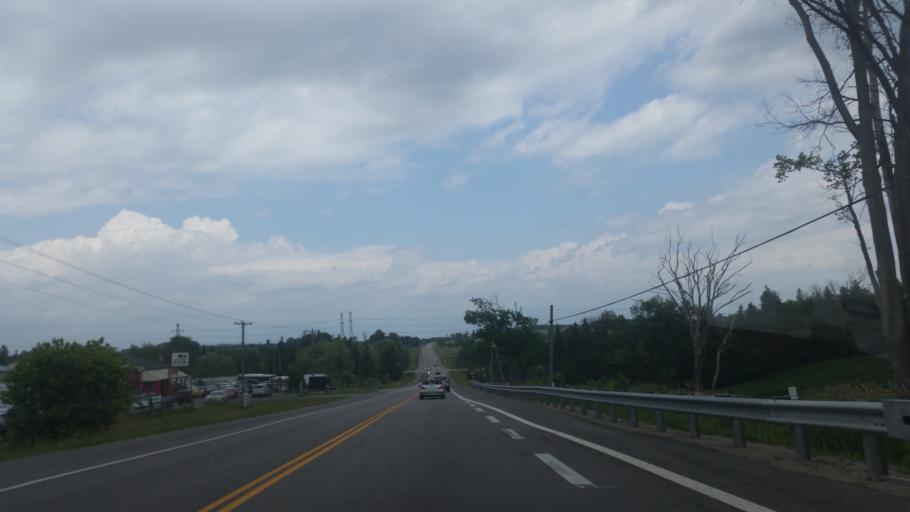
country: CA
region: Ontario
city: Orangeville
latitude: 43.7153
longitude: -80.1151
